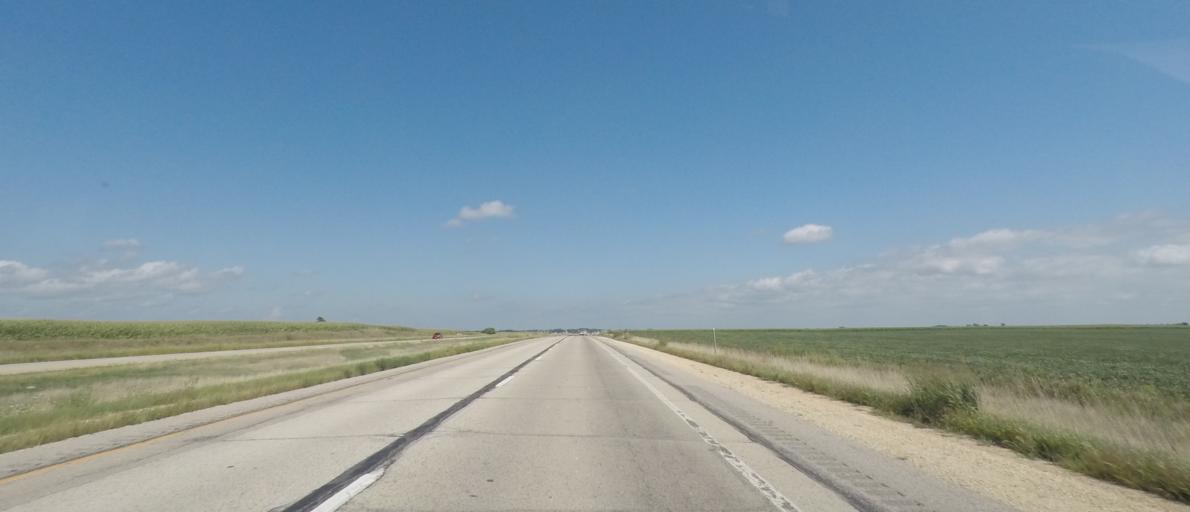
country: US
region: Iowa
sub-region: Linn County
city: Springville
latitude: 42.0687
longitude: -91.3740
